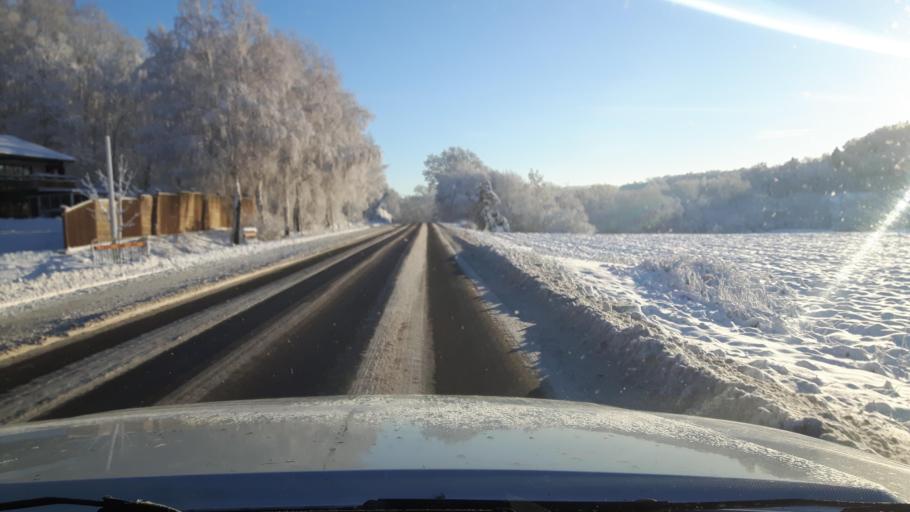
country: SE
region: Vaestra Goetaland
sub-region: Molndal
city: Lindome
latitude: 57.5427
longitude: 12.1388
